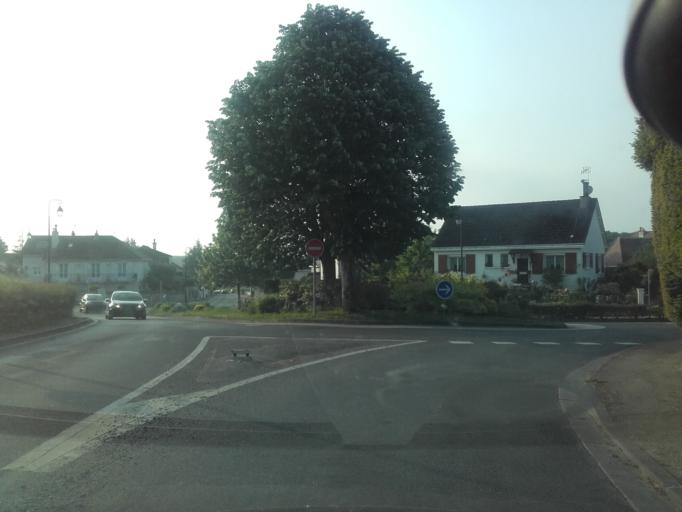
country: FR
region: Centre
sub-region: Departement d'Indre-et-Loire
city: Parcay-Meslay
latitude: 47.4430
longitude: 0.7482
